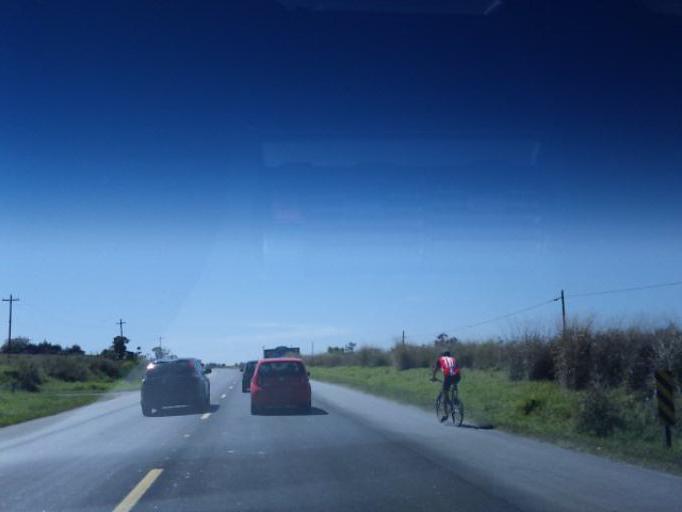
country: BR
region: Sao Paulo
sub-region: Tremembe
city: Tremembe
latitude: -22.9431
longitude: -45.6031
